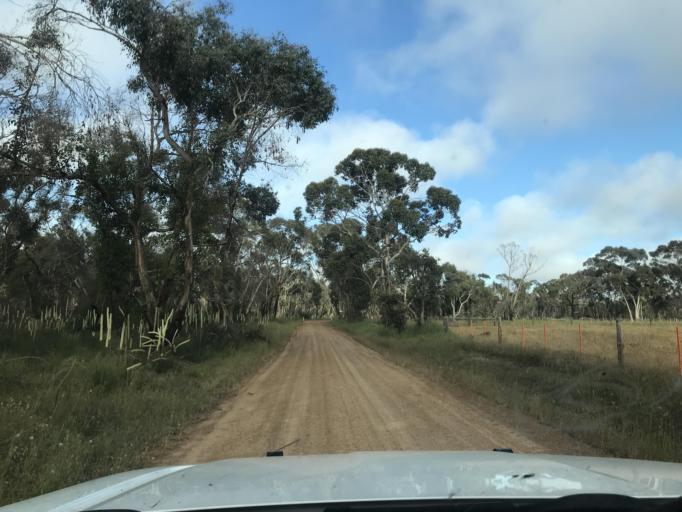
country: AU
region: South Australia
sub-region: Wattle Range
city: Penola
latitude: -37.1812
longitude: 141.1759
